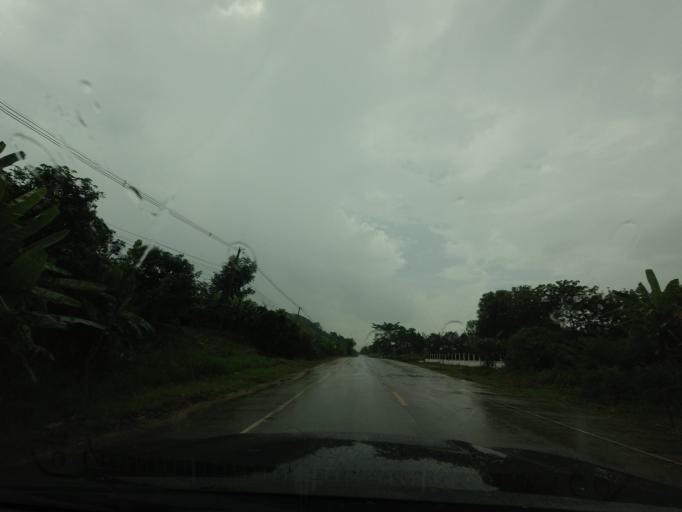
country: TH
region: Loei
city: Pak Chom
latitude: 18.1022
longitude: 101.9681
